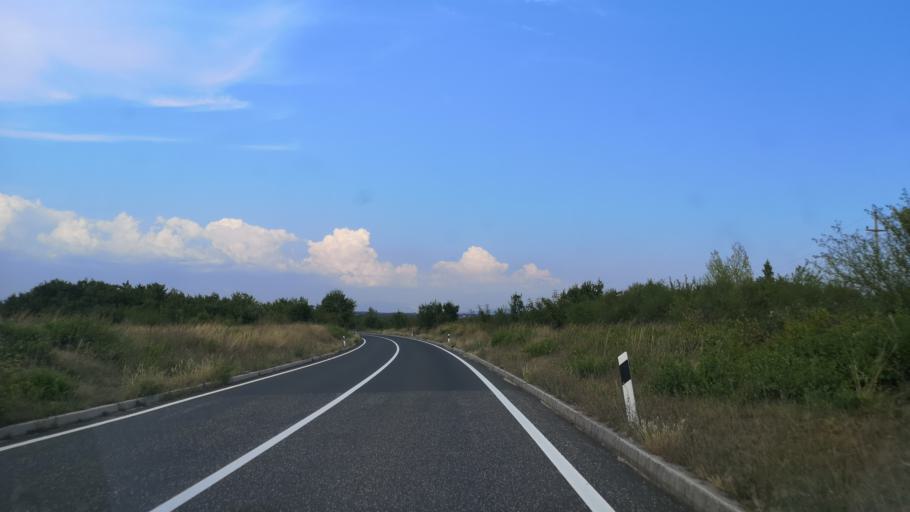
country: HR
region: Sibensko-Kniniska
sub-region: Grad Sibenik
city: Pirovac
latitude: 43.8782
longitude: 15.7492
